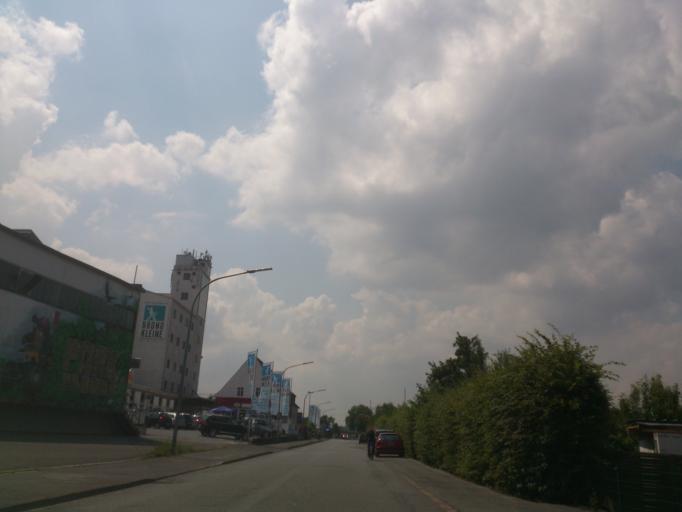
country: DE
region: North Rhine-Westphalia
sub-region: Regierungsbezirk Detmold
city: Paderborn
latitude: 51.7084
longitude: 8.7241
